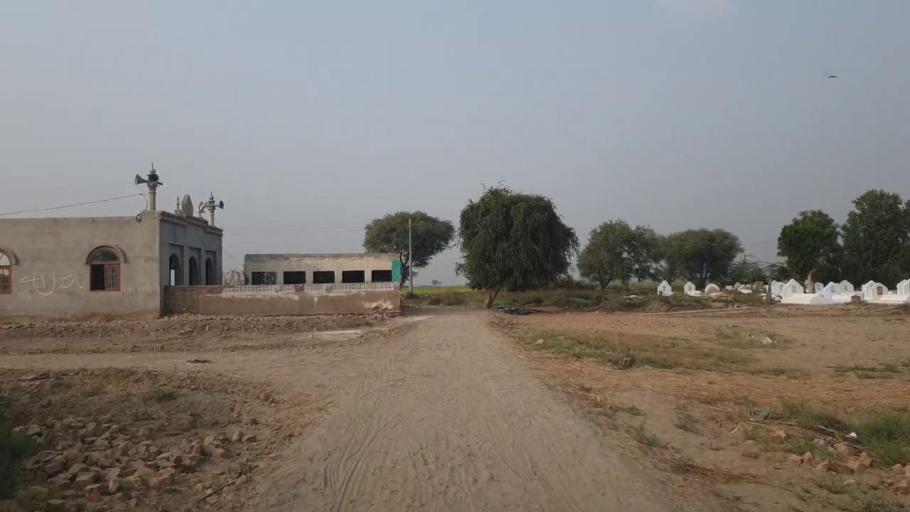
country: PK
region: Sindh
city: Mirpur Batoro
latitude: 24.5697
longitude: 68.4169
